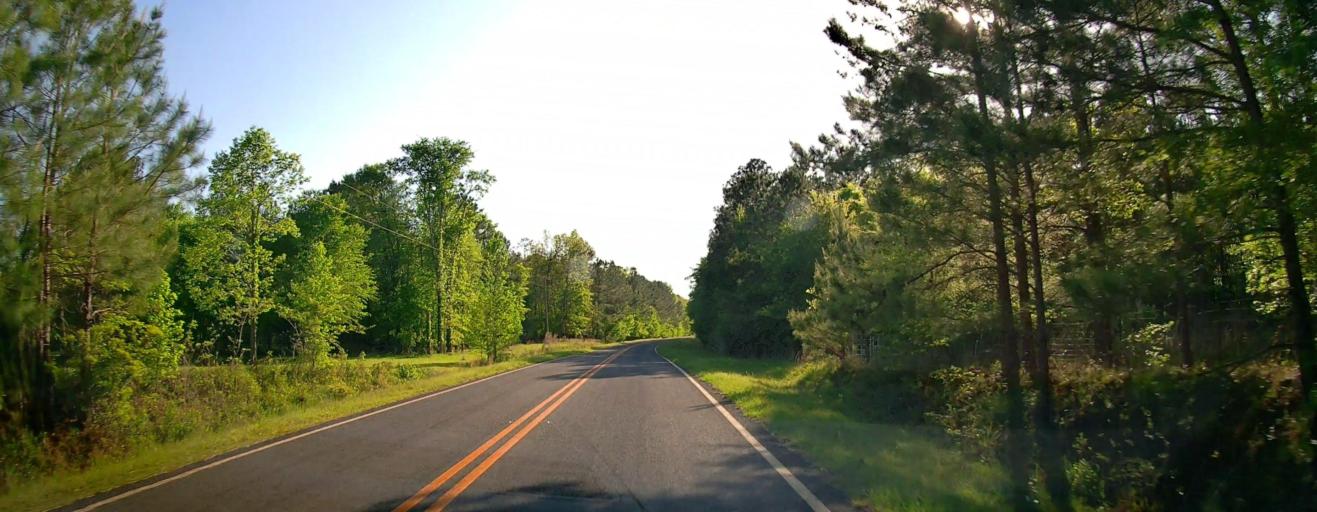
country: US
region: Georgia
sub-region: Macon County
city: Marshallville
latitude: 32.3863
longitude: -83.8554
